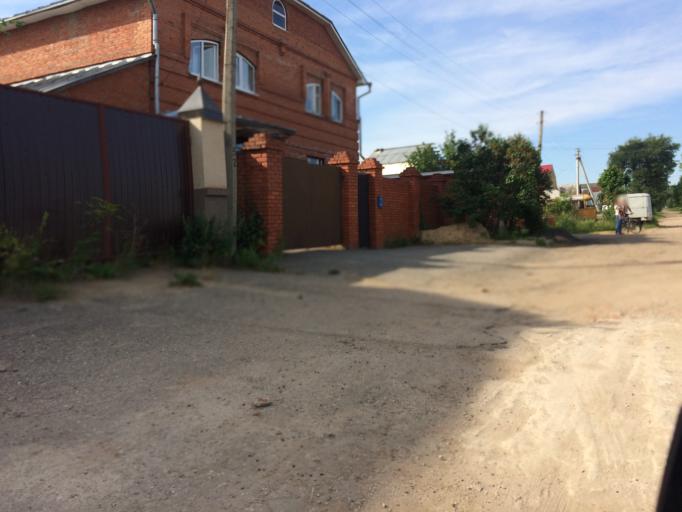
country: RU
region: Mariy-El
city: Yoshkar-Ola
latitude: 56.6508
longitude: 47.9187
